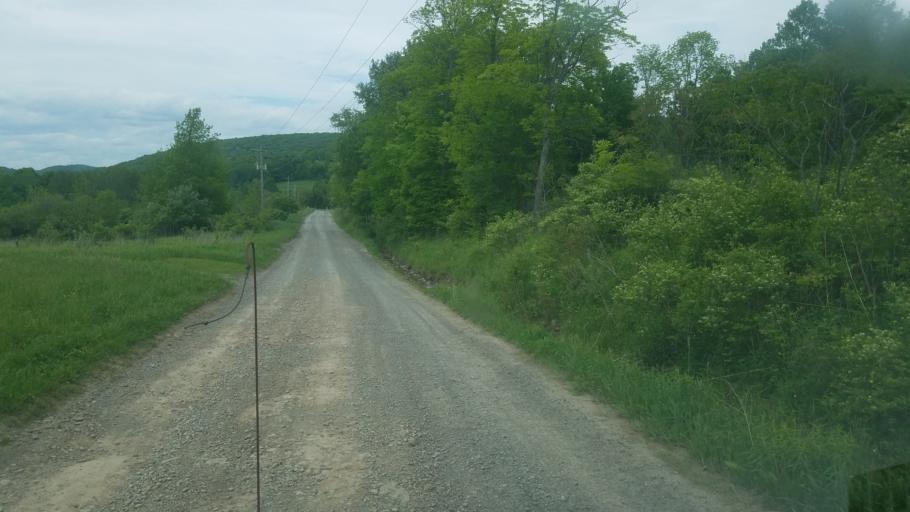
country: US
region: Pennsylvania
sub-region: Tioga County
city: Westfield
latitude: 41.8790
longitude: -77.5961
